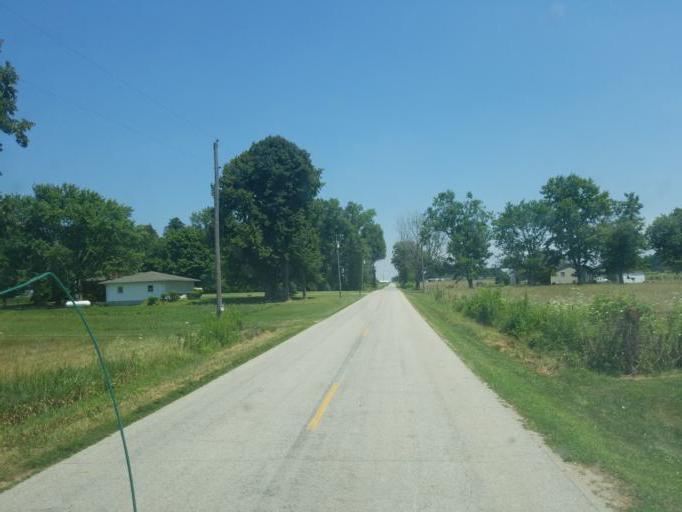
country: US
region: Ohio
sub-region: Shelby County
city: Botkins
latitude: 40.4823
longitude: -84.1953
